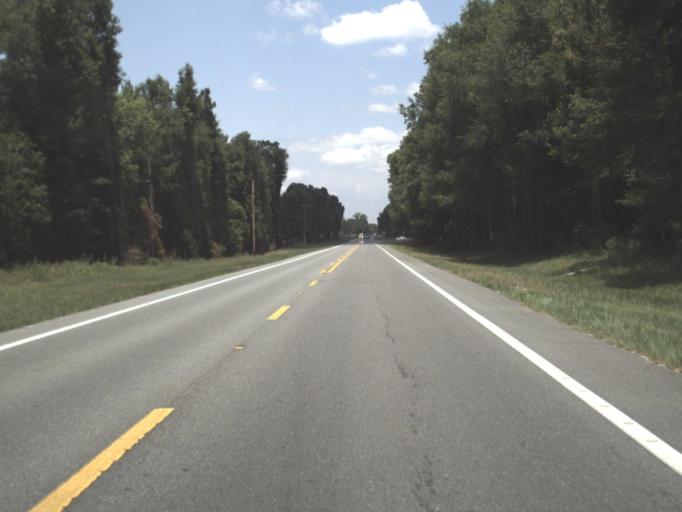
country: US
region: Florida
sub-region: Levy County
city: Williston
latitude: 29.4125
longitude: -82.4319
